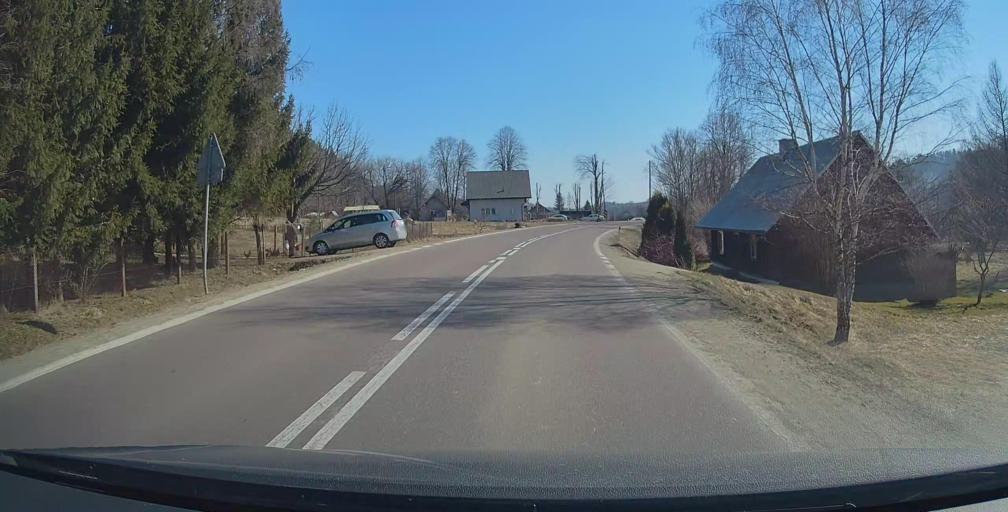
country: PL
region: Subcarpathian Voivodeship
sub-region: Powiat przemyski
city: Bircza
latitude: 49.5838
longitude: 22.5352
